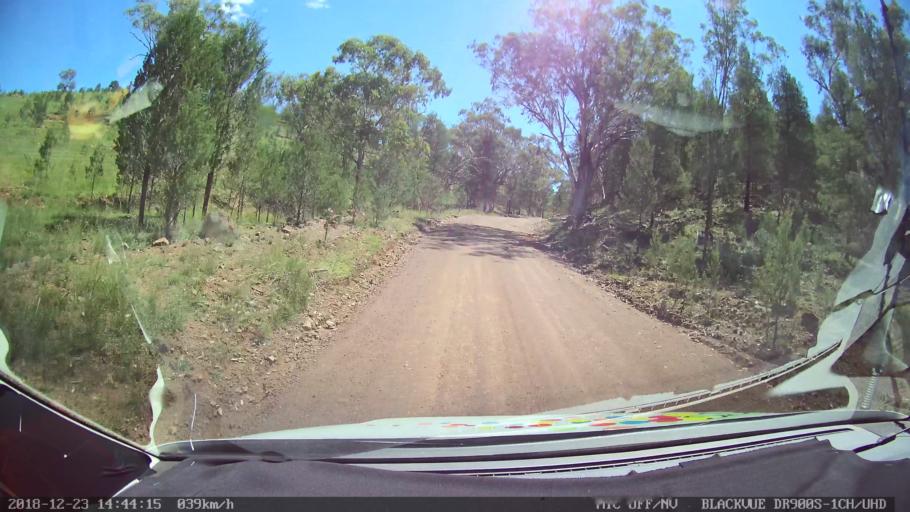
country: AU
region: New South Wales
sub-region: Tamworth Municipality
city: Manilla
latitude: -30.6460
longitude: 150.8972
